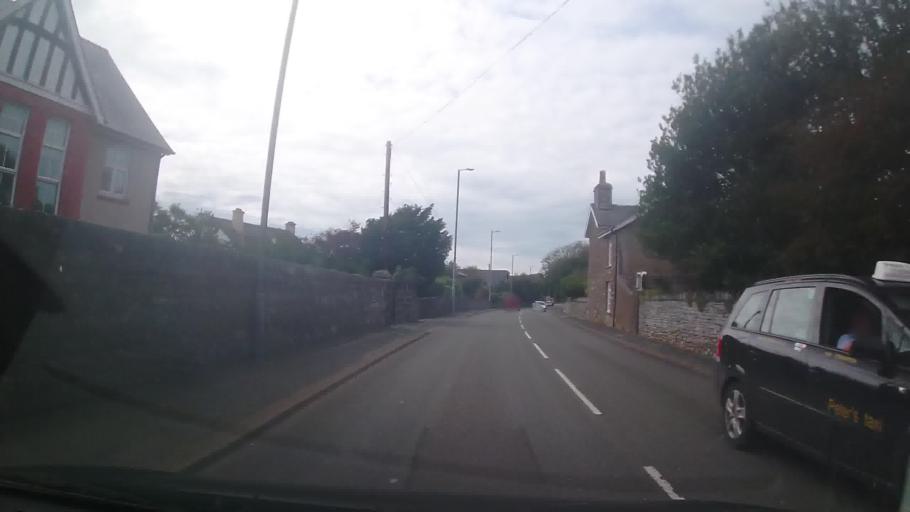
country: GB
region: Wales
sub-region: Gwynedd
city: Tywyn
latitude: 52.5834
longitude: -4.0858
